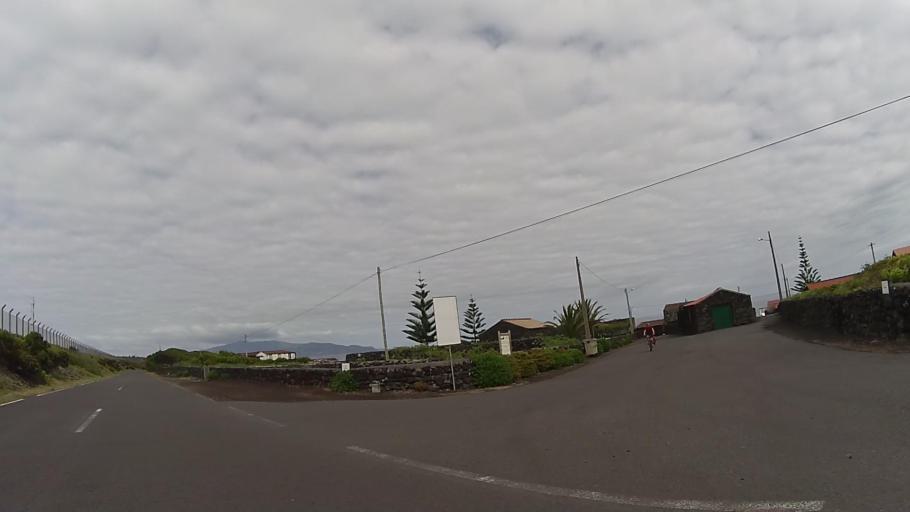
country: PT
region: Azores
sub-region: Madalena
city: Madalena
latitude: 38.5547
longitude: -28.4456
